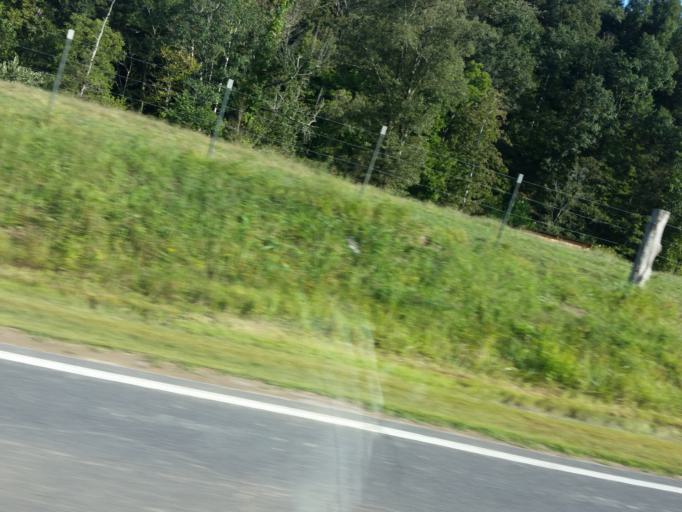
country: US
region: Tennessee
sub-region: Union County
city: Luttrell
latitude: 36.2310
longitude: -83.7607
